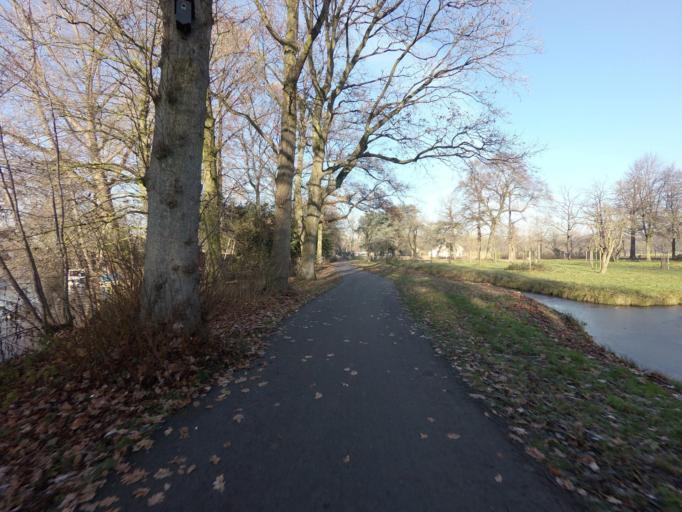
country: NL
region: Utrecht
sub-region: Gemeente Woerden
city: Woerden
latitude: 52.0894
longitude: 4.8894
